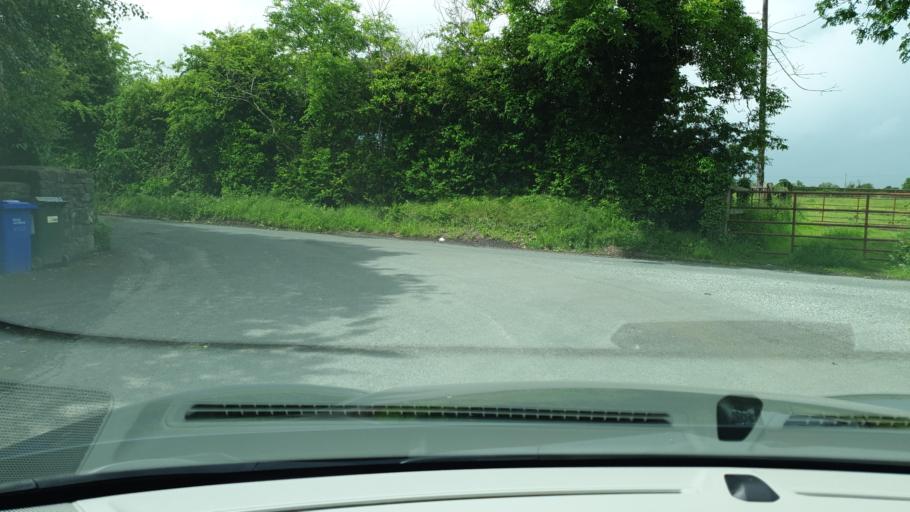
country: IE
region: Leinster
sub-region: Kildare
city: Celbridge
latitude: 53.3674
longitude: -6.5355
